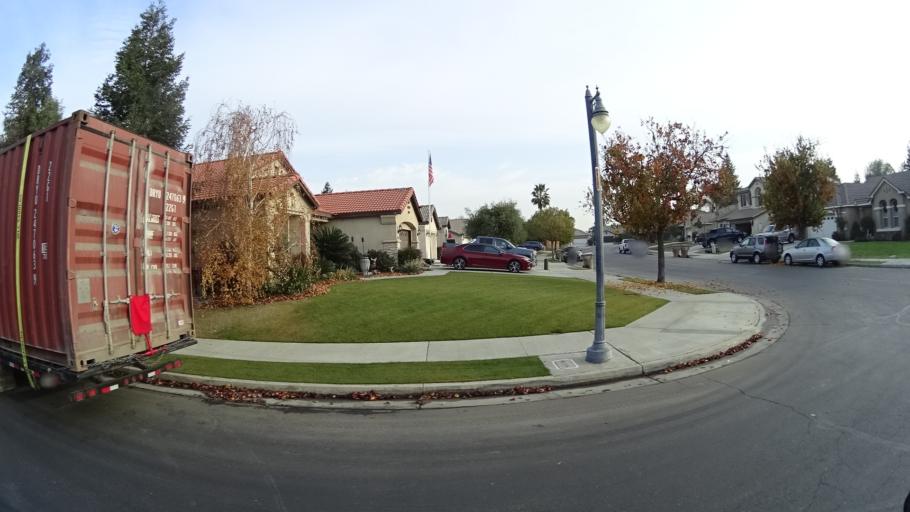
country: US
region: California
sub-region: Kern County
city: Greenacres
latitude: 35.4172
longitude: -119.1189
